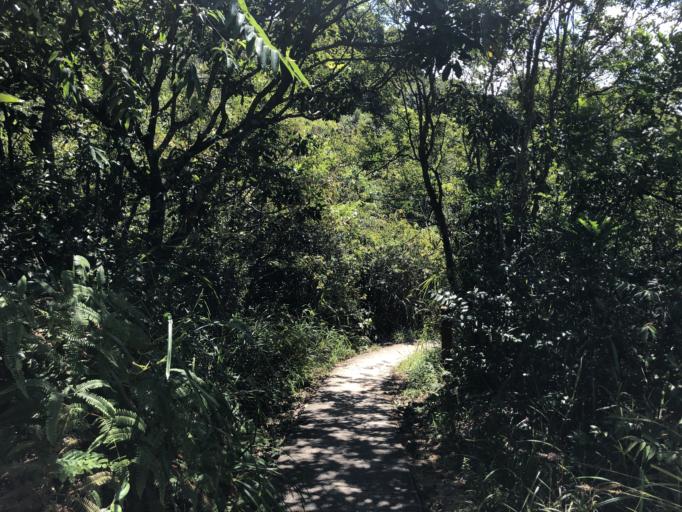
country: HK
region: Tuen Mun
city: Tuen Mun
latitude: 22.2843
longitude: 113.9826
